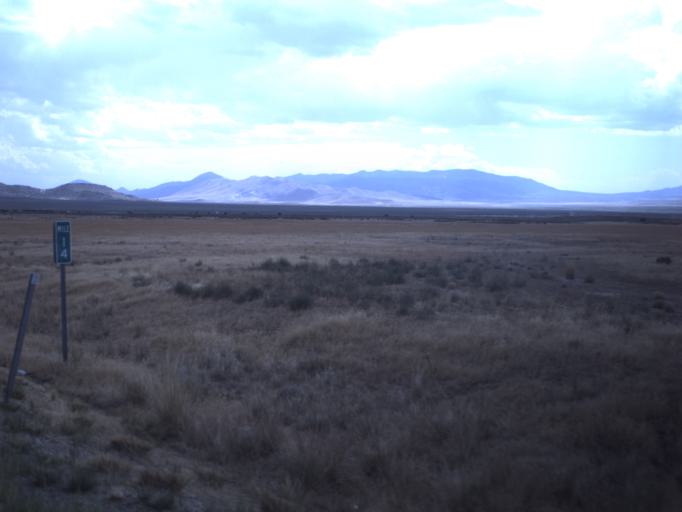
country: US
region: Utah
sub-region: Utah County
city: Eagle Mountain
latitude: 40.2425
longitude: -112.2075
